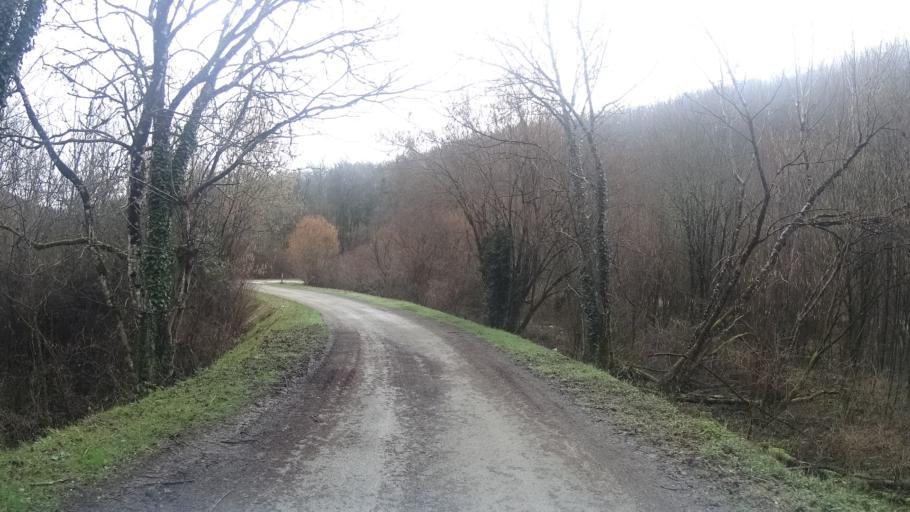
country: FR
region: Aquitaine
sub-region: Departement de la Dordogne
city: Terrasson-Lavilledieu
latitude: 45.1041
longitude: 1.2575
